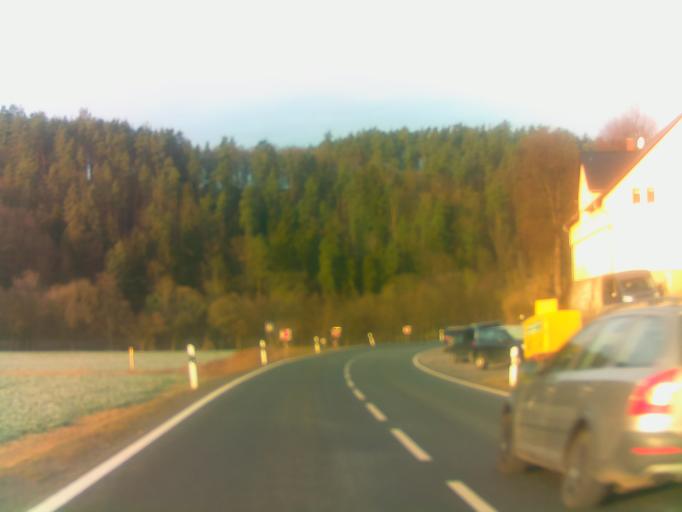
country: DE
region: Thuringia
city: Freienorla
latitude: 50.7564
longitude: 11.5478
